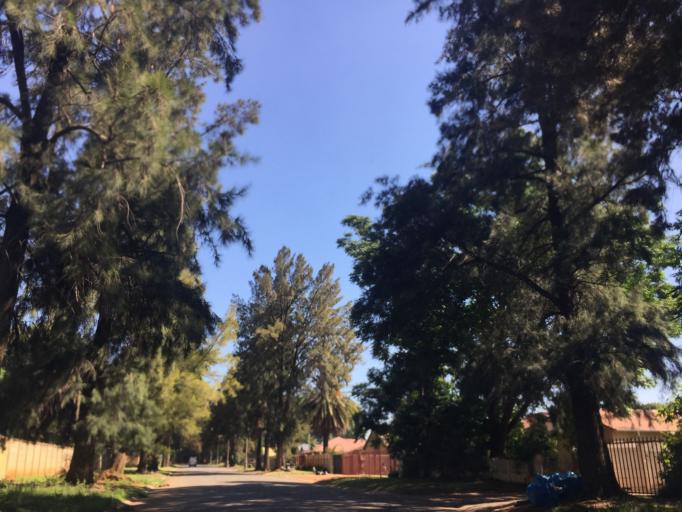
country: ZA
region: Gauteng
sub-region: Sedibeng District Municipality
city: Vanderbijlpark
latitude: -26.7029
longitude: 27.8449
